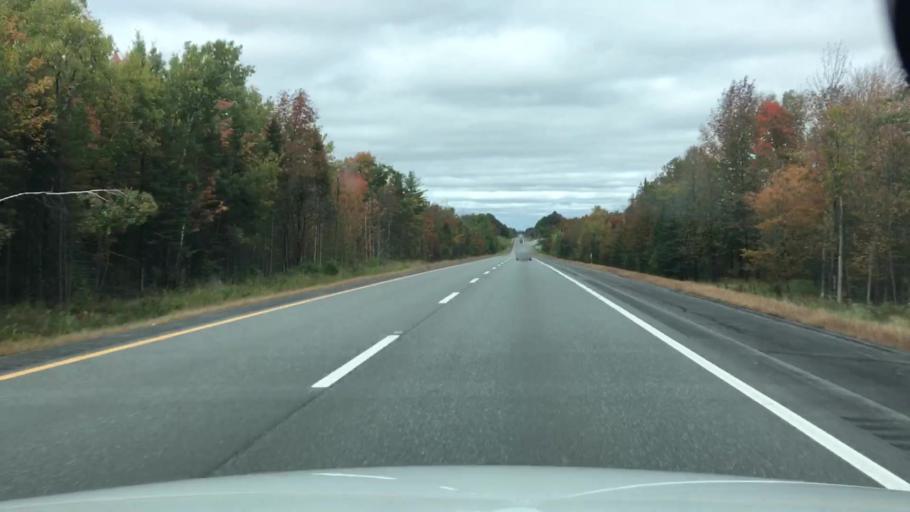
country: US
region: Maine
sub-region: Waldo County
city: Burnham
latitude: 44.7380
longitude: -69.4306
